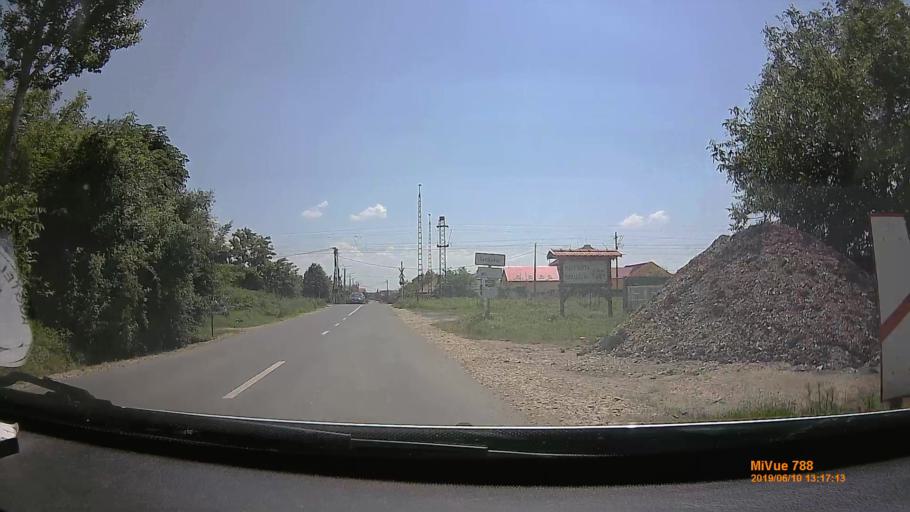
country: HU
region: Borsod-Abauj-Zemplen
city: Tiszaluc
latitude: 48.0400
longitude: 21.0622
